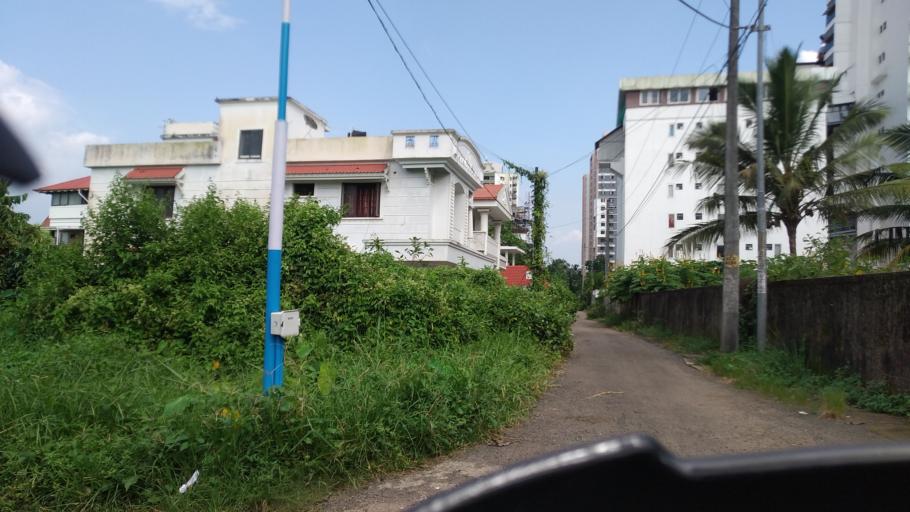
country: IN
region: Kerala
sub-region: Ernakulam
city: Cochin
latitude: 9.9888
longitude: 76.3000
